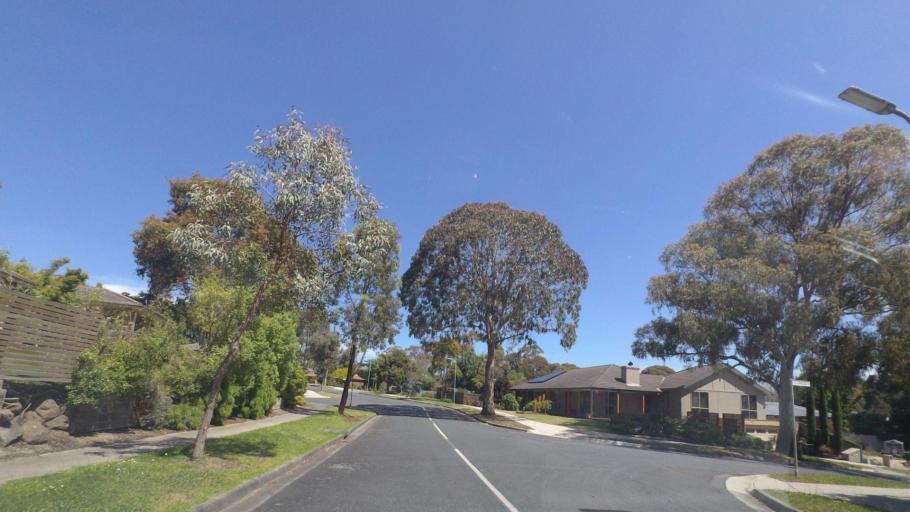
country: AU
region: Victoria
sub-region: Whitehorse
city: Vermont
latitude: -37.8485
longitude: 145.1939
